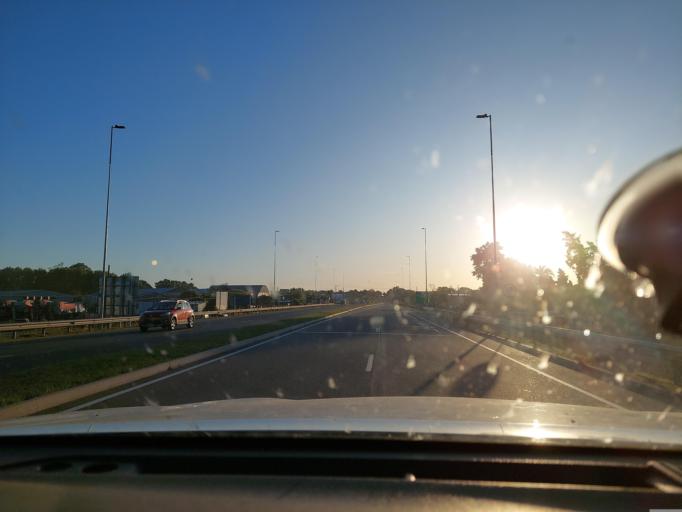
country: UY
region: Canelones
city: Pando
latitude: -34.7151
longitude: -55.9459
